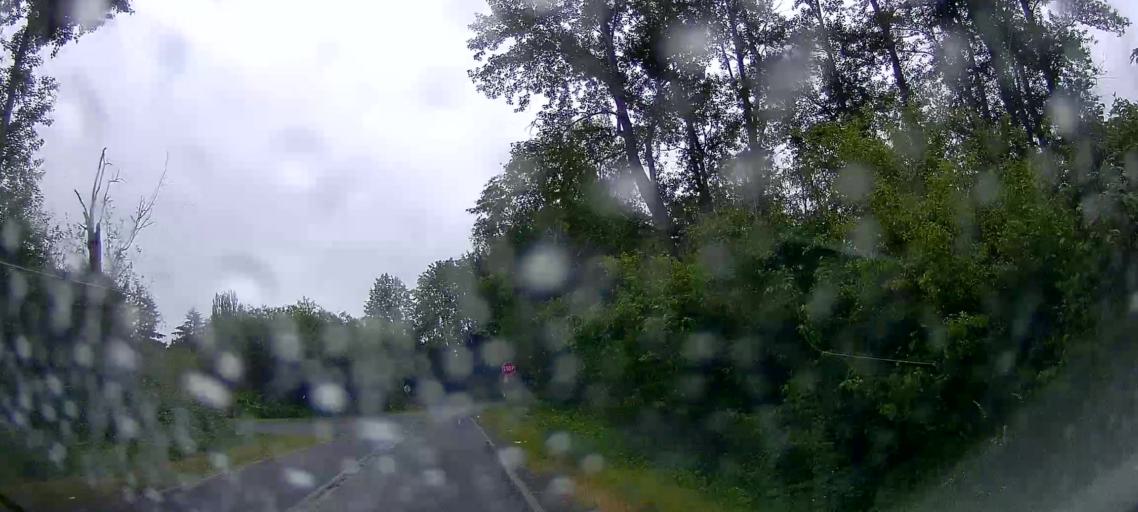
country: US
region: Washington
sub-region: Whatcom County
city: Marietta
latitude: 48.7901
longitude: -122.5815
